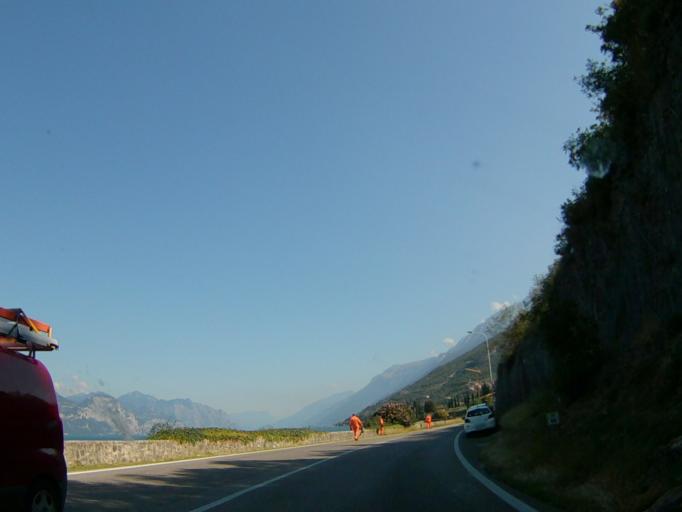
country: IT
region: Veneto
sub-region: Provincia di Verona
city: San Zeno
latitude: 45.6427
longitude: 10.7108
